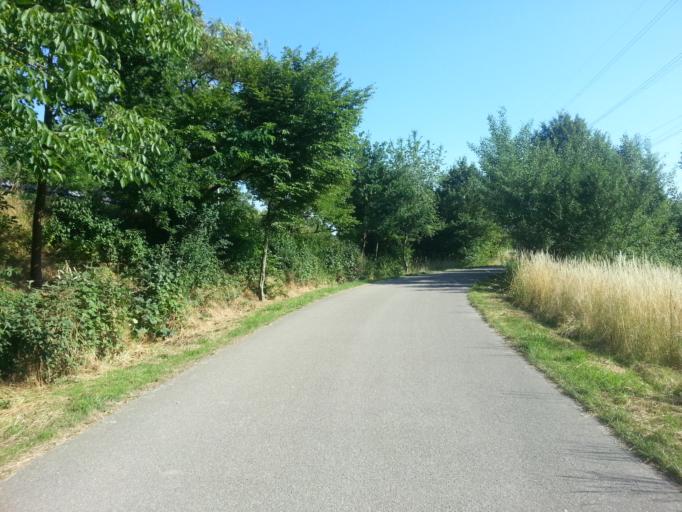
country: DE
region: Hesse
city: Viernheim
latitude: 49.5366
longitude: 8.5576
